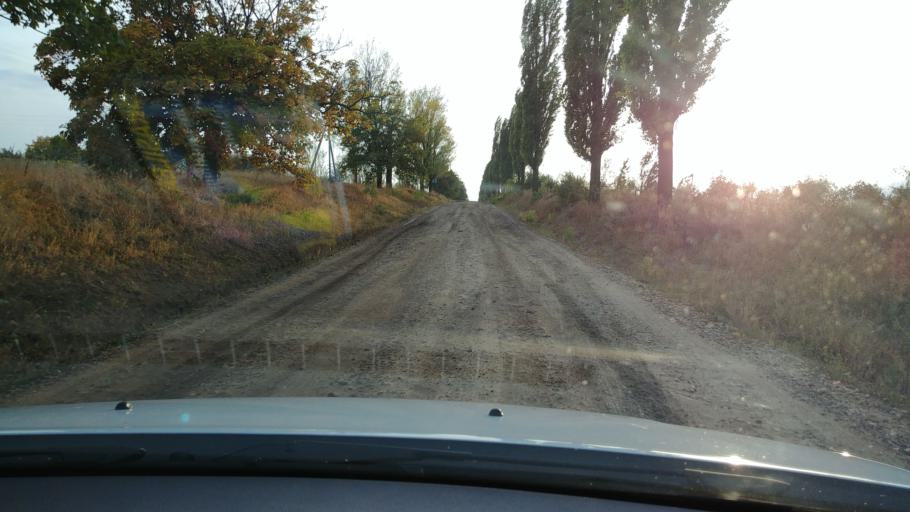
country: MD
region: Rezina
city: Saharna
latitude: 47.6806
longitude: 28.9711
